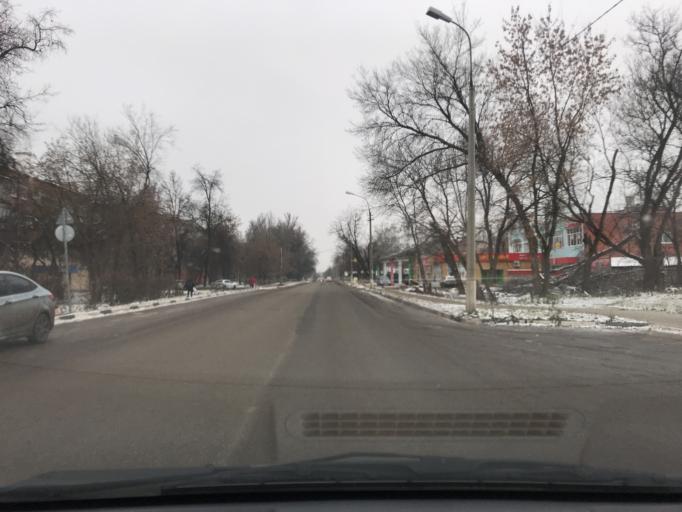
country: RU
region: Moskovskaya
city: Elektrostal'
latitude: 55.7957
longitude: 38.4446
